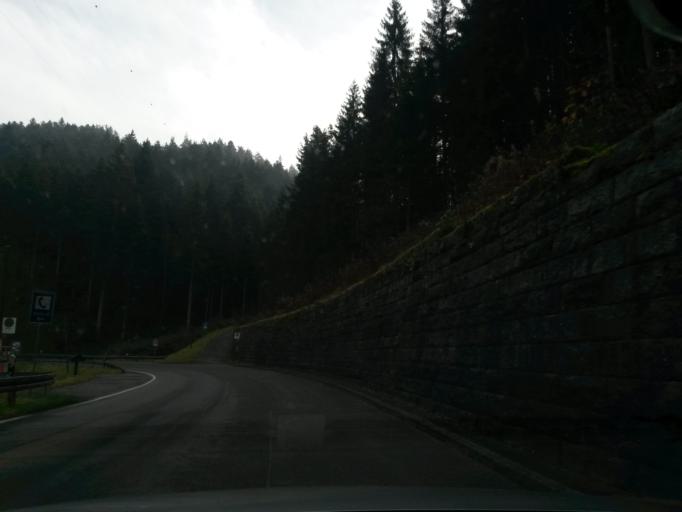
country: DE
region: Baden-Wuerttemberg
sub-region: Freiburg Region
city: Hardt
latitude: 48.1882
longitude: 8.3865
